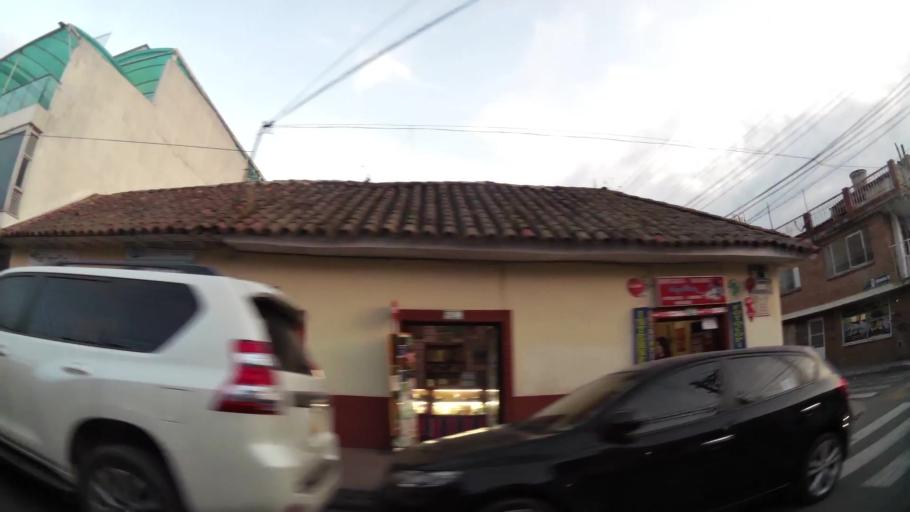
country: CO
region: Cundinamarca
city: Funza
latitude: 4.7148
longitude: -74.2129
